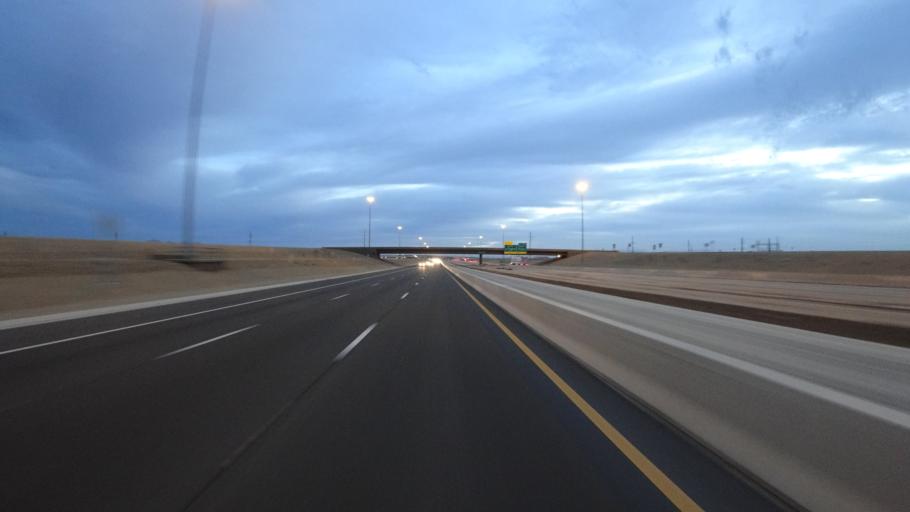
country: US
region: Arizona
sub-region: Maricopa County
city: Litchfield Park
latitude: 33.4810
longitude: -112.4233
